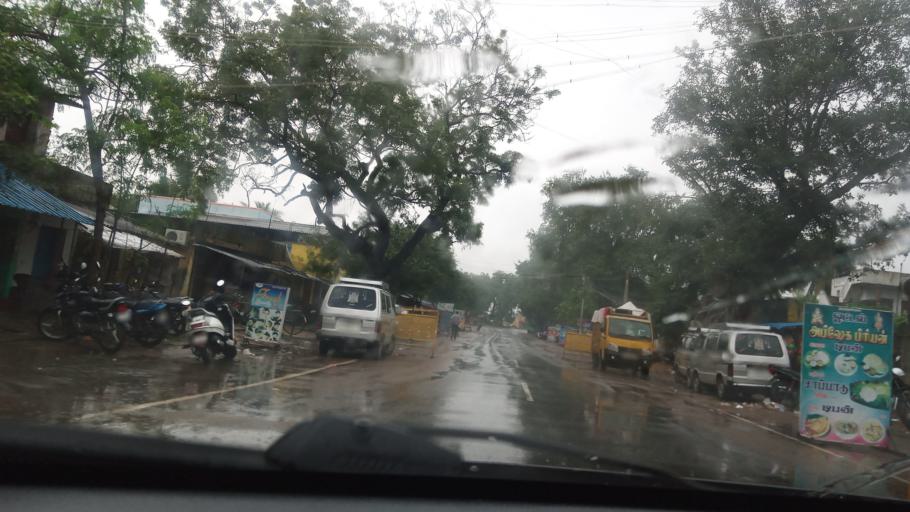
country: IN
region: Tamil Nadu
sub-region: Vellore
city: Kalavai
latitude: 12.8050
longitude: 79.4166
